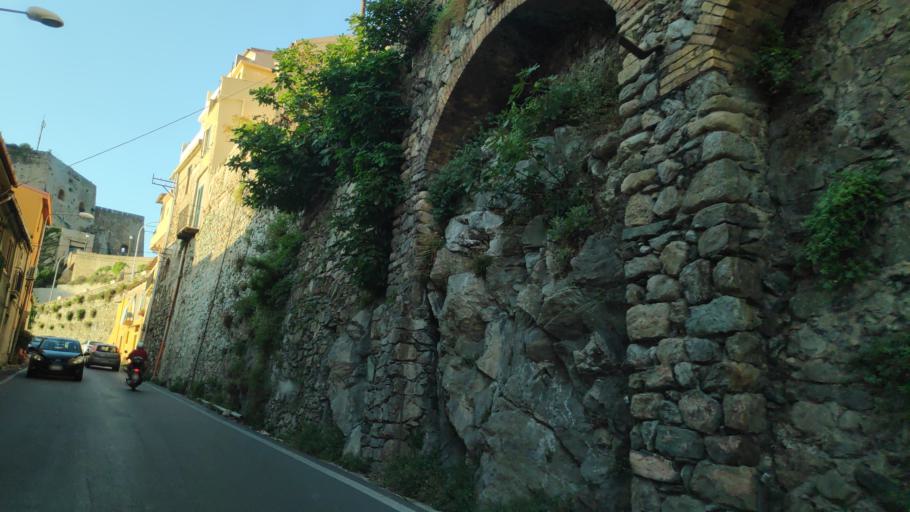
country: IT
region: Calabria
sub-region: Provincia di Reggio Calabria
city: Scilla
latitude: 38.2545
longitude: 15.7152
